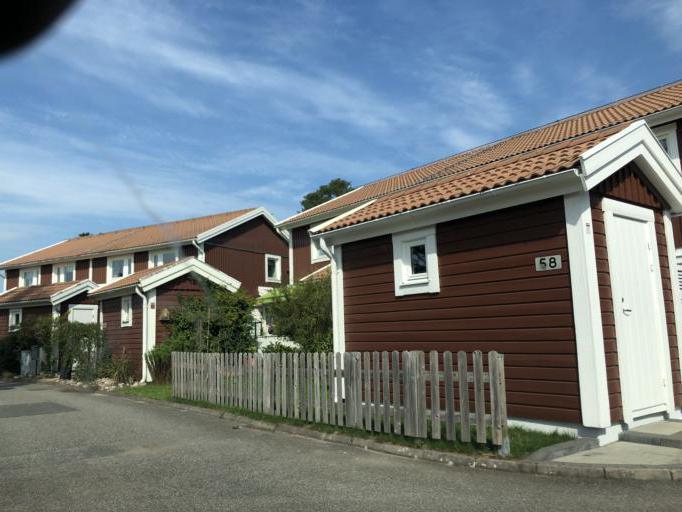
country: SE
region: Vaestra Goetaland
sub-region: Goteborg
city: Goeteborg
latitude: 57.7627
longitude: 11.9679
